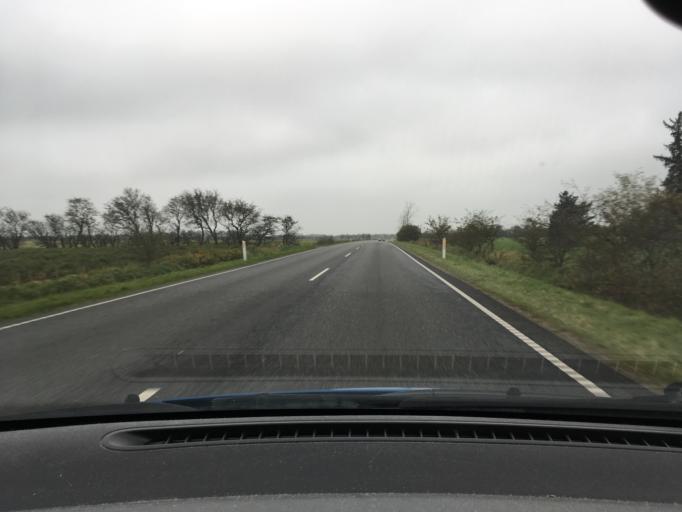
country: DK
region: South Denmark
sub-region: Tonder Kommune
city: Toftlund
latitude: 55.0577
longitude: 9.1248
